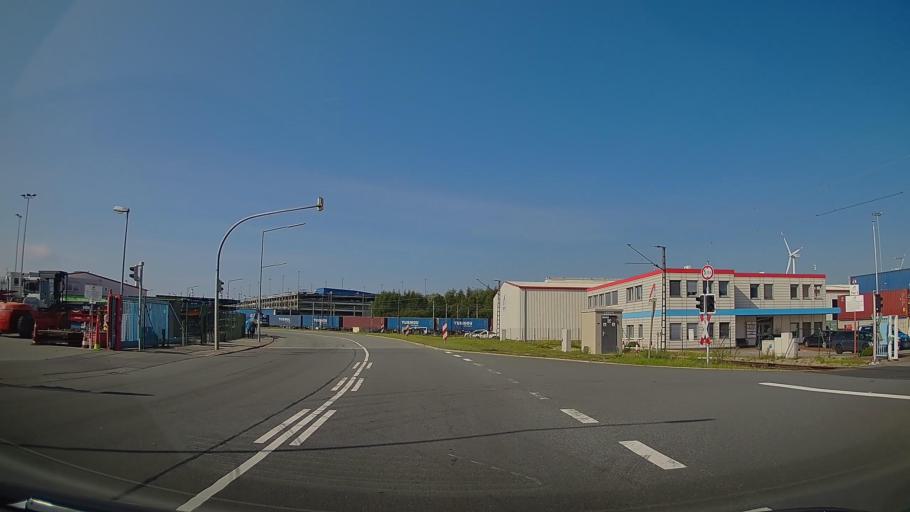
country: DE
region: Bremen
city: Bremerhaven
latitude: 53.5782
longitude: 8.5619
